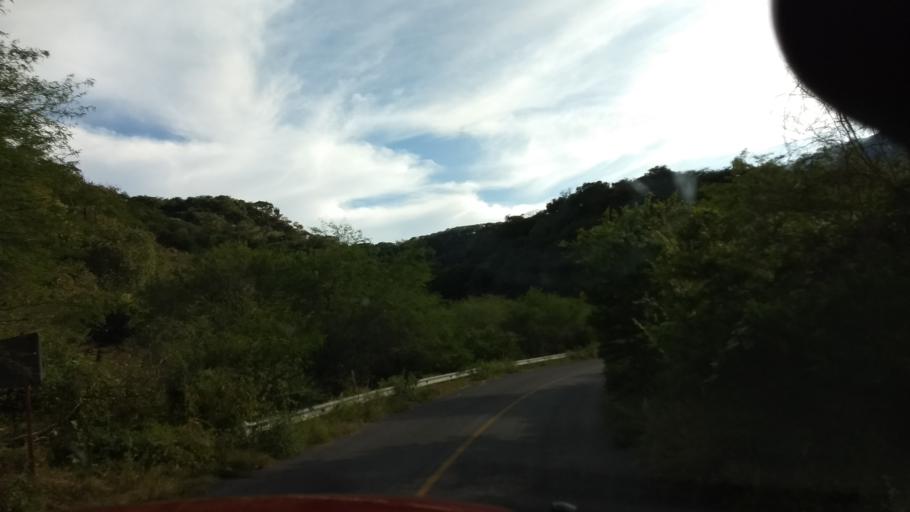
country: MX
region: Colima
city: Suchitlan
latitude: 19.4562
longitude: -103.8231
